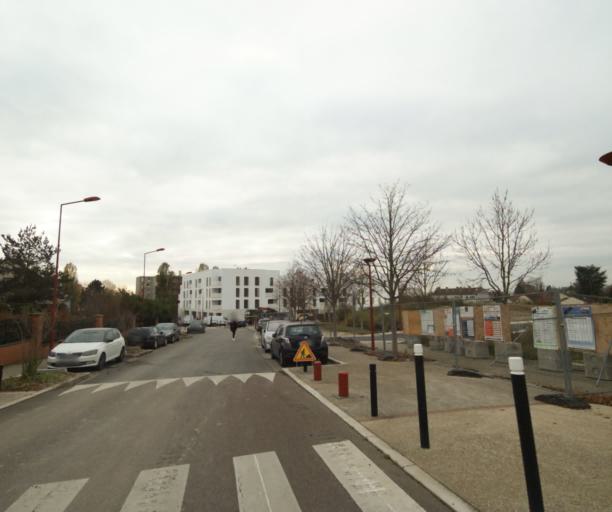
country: FR
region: Ile-de-France
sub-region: Departement du Val-d'Oise
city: Arnouville
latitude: 48.9836
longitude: 2.4320
